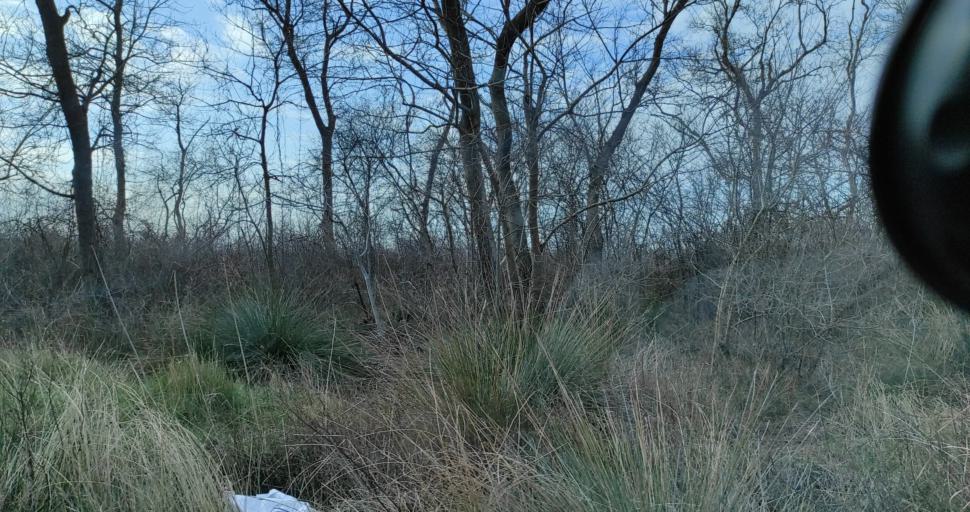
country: AL
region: Lezhe
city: Shengjin
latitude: 41.7747
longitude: 19.6030
